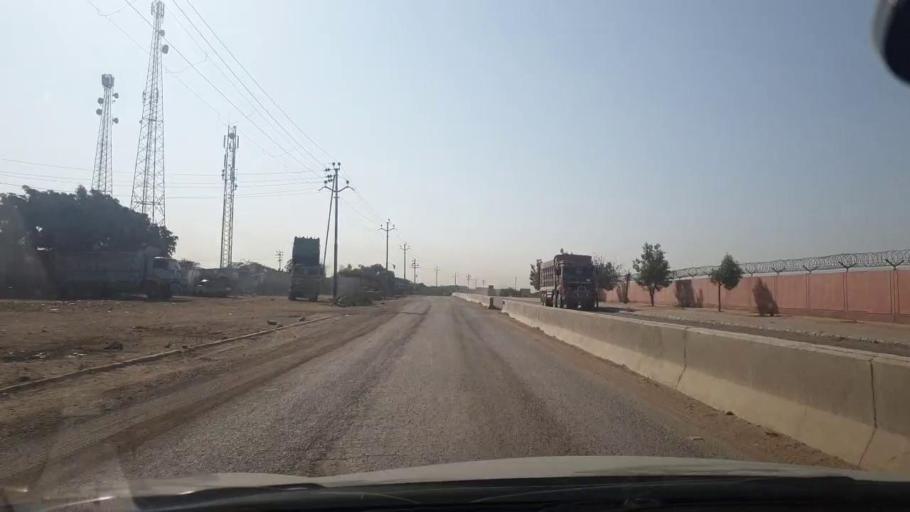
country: PK
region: Sindh
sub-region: Karachi District
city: Karachi
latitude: 25.0794
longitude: 67.0134
